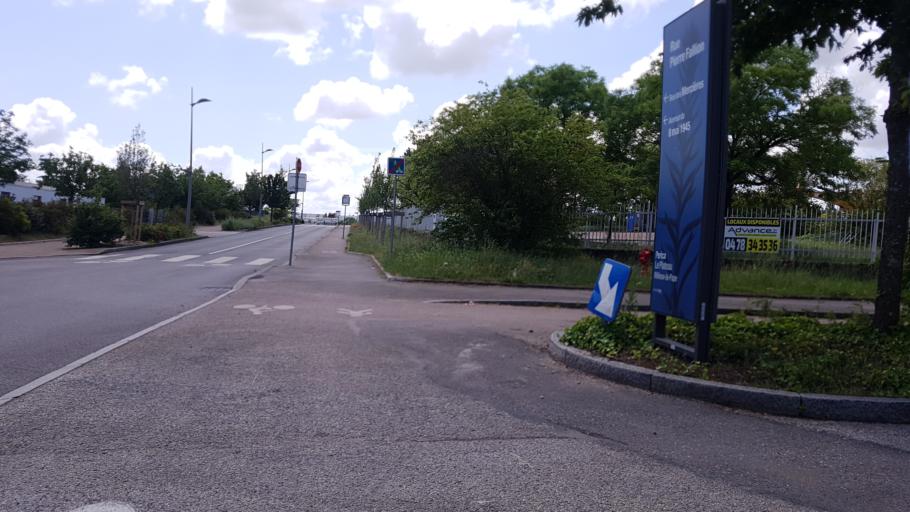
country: FR
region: Rhone-Alpes
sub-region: Departement du Rhone
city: Sathonay-Camp
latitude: 45.8167
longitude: 4.8726
